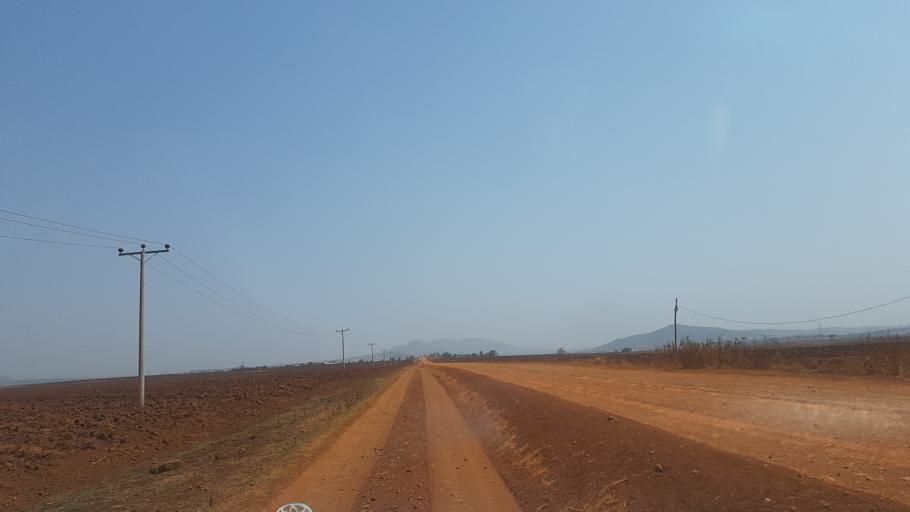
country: ET
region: Oromiya
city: Shambu
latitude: 9.4005
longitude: 36.5382
